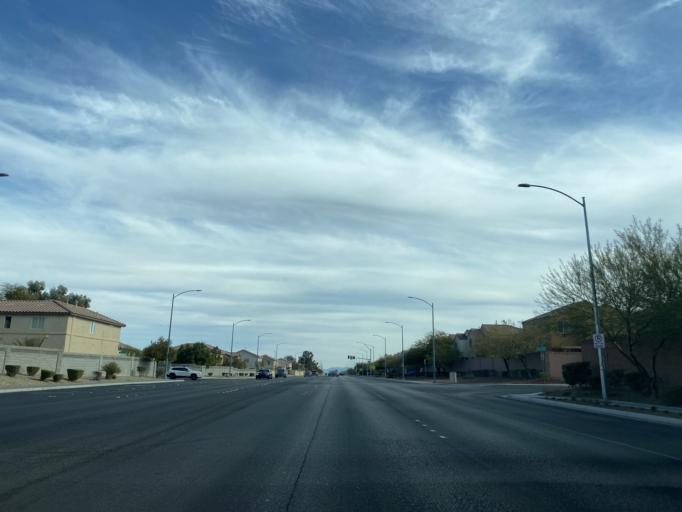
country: US
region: Nevada
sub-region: Clark County
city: Enterprise
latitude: 36.0556
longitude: -115.2957
